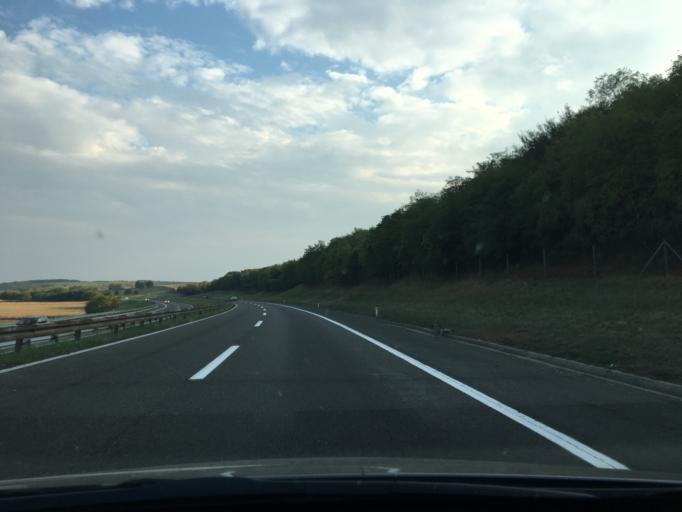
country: RS
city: Lugavcina
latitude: 44.4933
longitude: 21.0222
